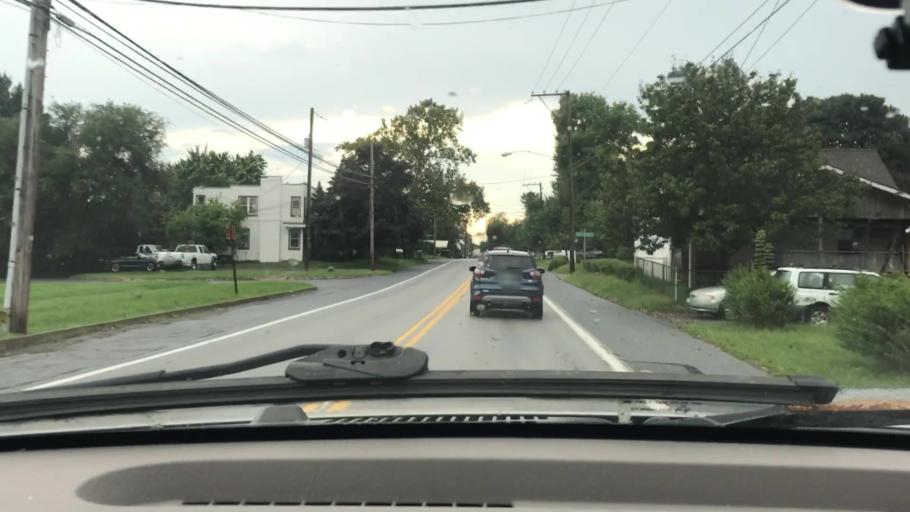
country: US
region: Pennsylvania
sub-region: Dauphin County
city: Colonial Park
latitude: 40.2932
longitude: -76.7986
